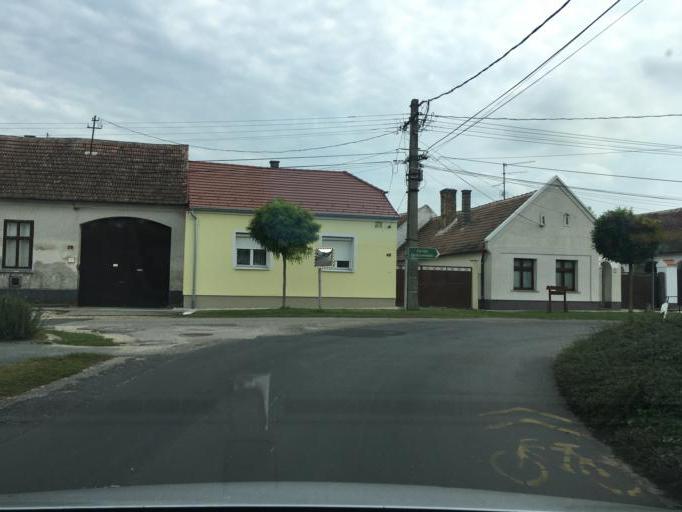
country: HU
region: Gyor-Moson-Sopron
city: Fertod
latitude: 47.6357
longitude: 16.8640
